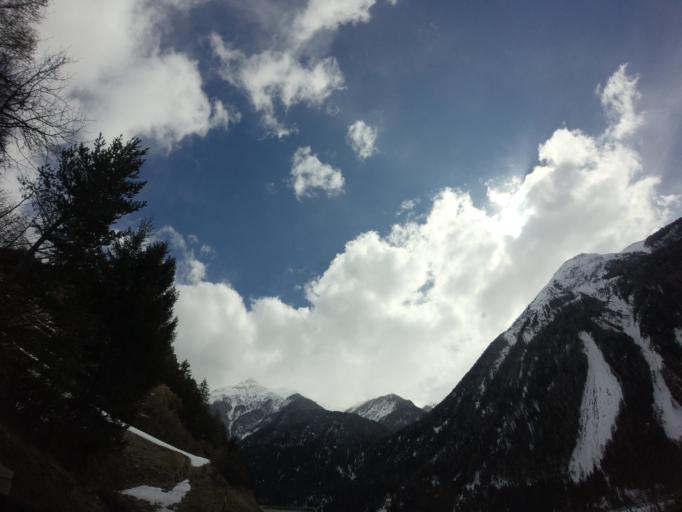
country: CH
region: Grisons
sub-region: Inn District
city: Scuol
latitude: 46.8338
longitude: 10.3913
